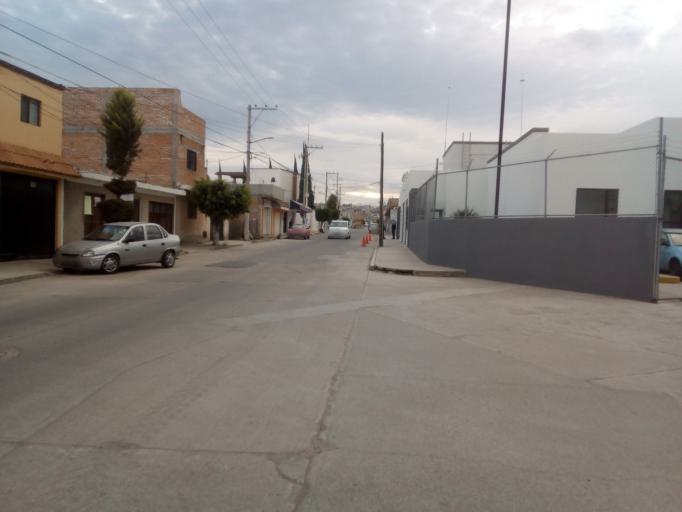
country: MX
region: Guanajuato
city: San Jose Iturbide
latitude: 21.0069
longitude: -100.3895
